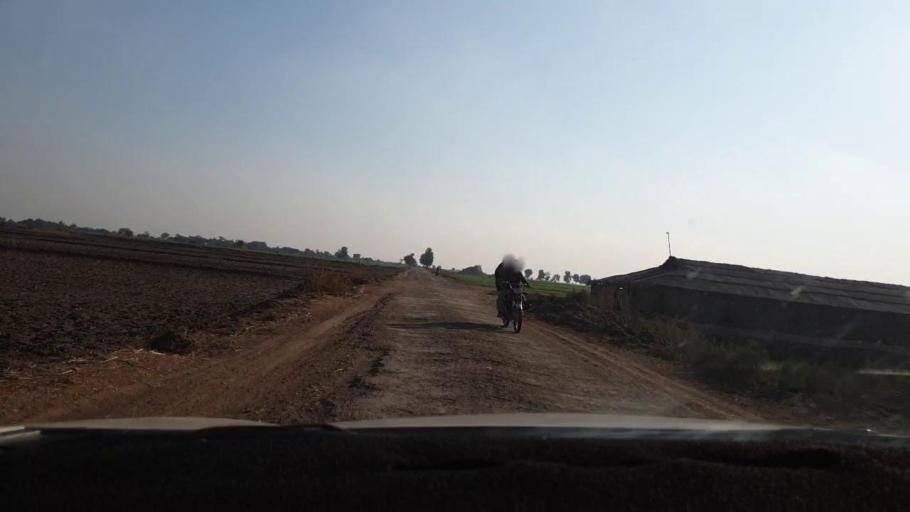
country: PK
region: Sindh
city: Berani
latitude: 25.7712
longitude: 68.7686
